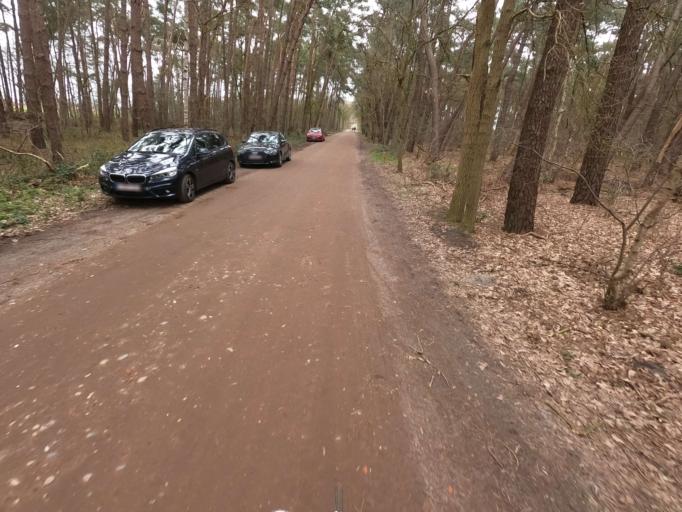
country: BE
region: Flanders
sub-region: Provincie Antwerpen
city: Kalmthout
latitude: 51.4193
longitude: 4.3970
